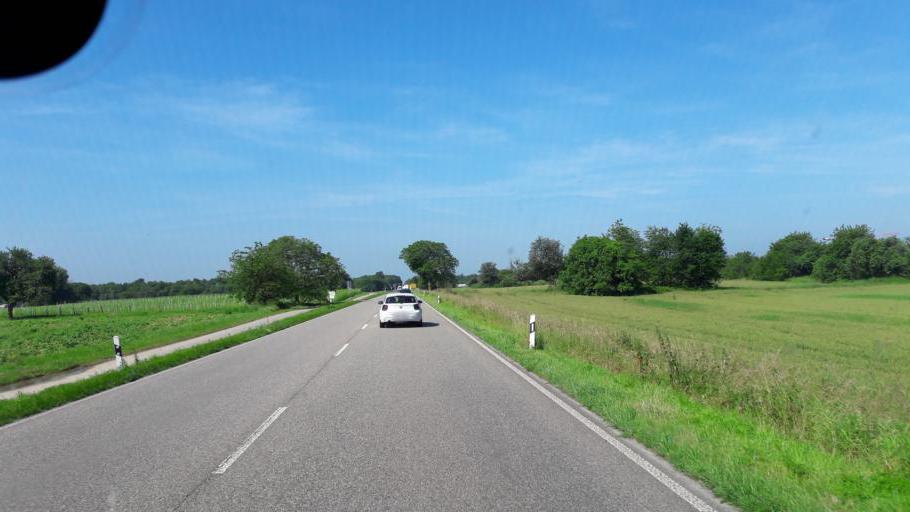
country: DE
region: Baden-Wuerttemberg
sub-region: Karlsruhe Region
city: Otigheim
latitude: 48.8780
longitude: 8.2518
